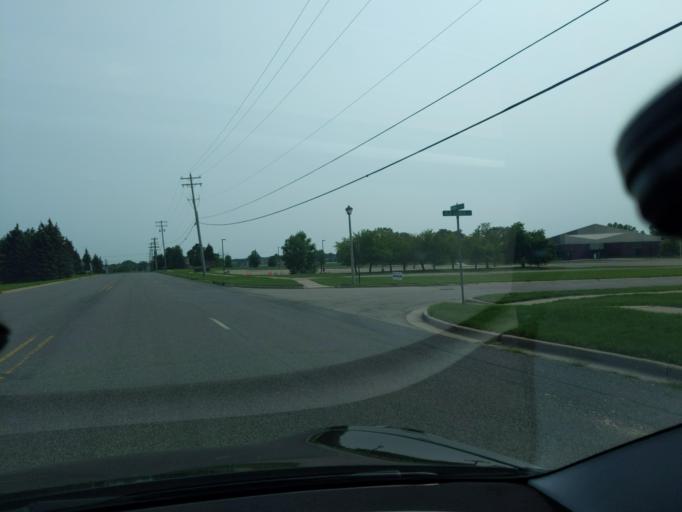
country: US
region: Michigan
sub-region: Ingham County
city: Holt
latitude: 42.6432
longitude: -84.5678
